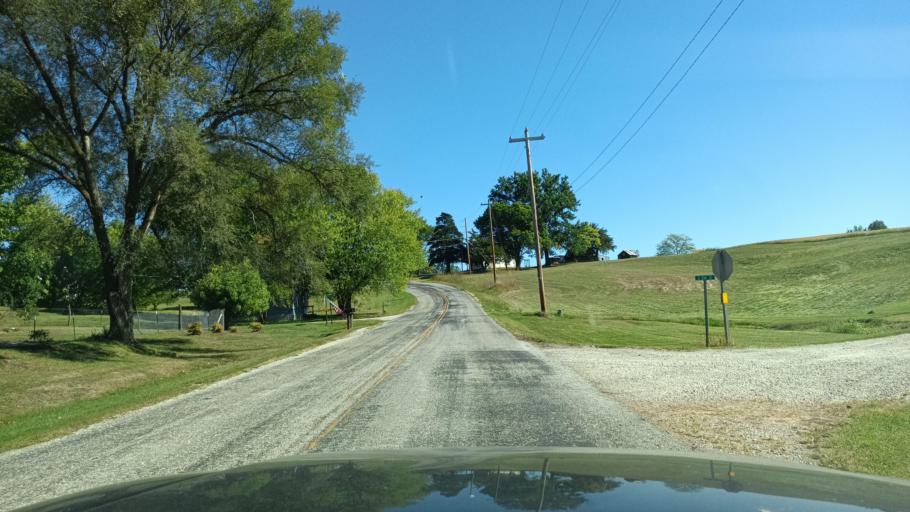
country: US
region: Missouri
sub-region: Macon County
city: La Plata
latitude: 39.9545
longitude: -92.6484
